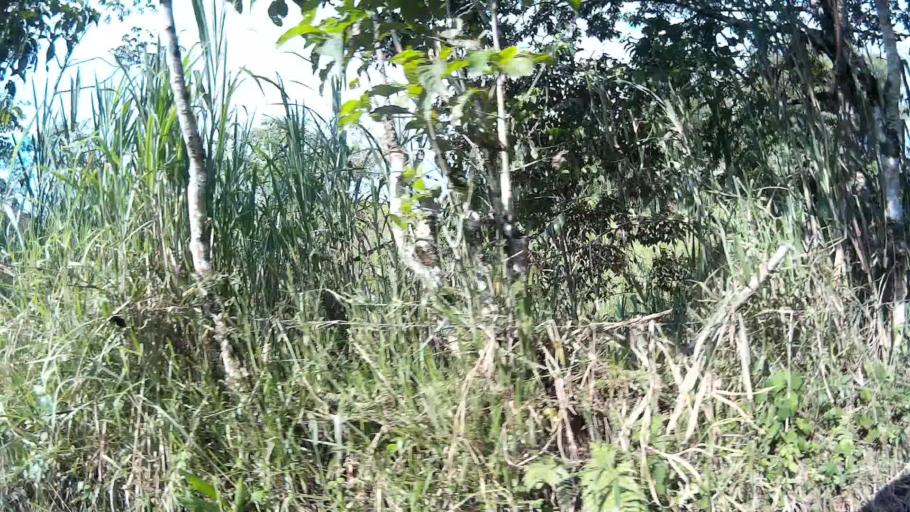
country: CO
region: Valle del Cauca
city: Ulloa
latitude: 4.7080
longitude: -75.6935
